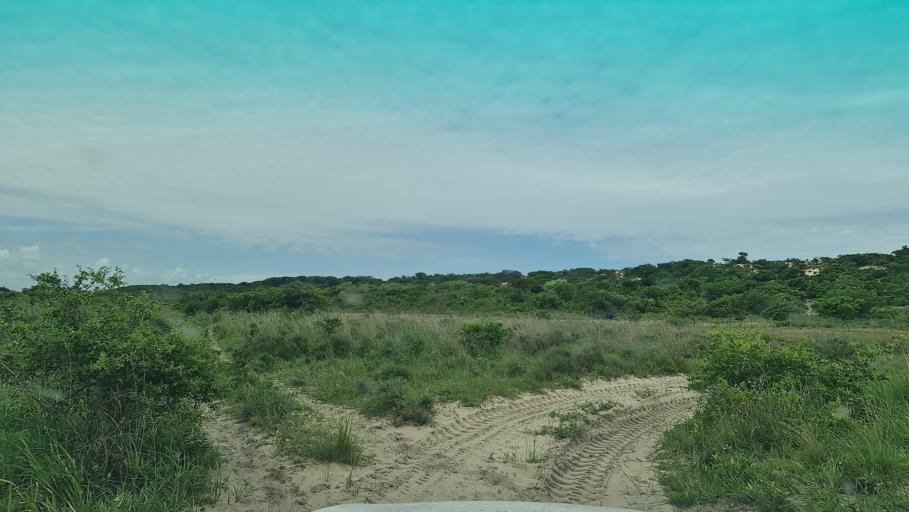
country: MZ
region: Maputo
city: Manhica
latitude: -25.6370
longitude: 32.7734
